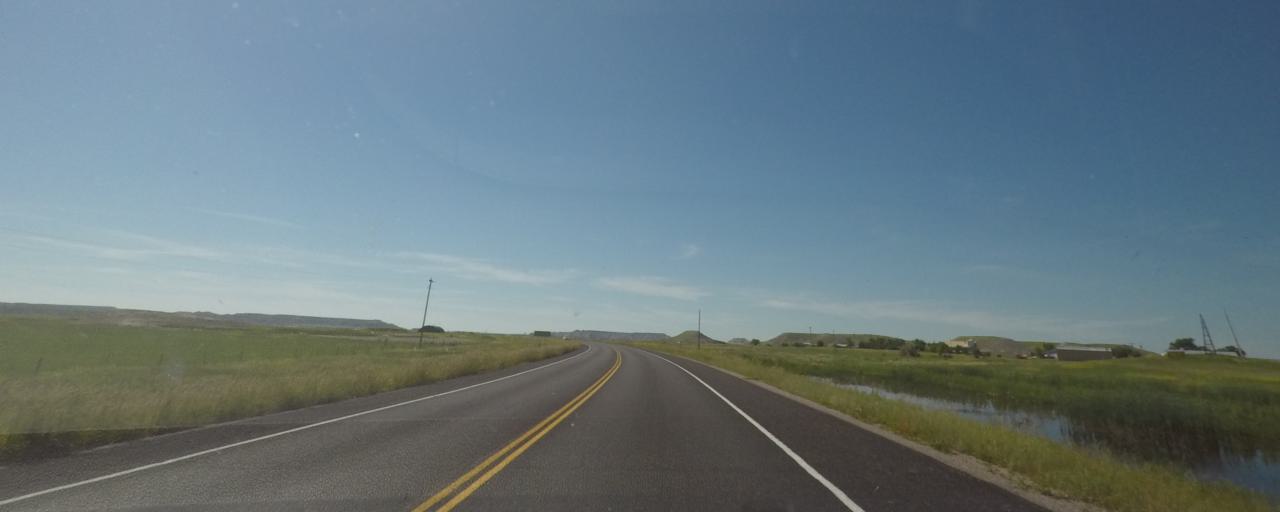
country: US
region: South Dakota
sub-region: Shannon County
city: Porcupine
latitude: 43.7834
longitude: -102.5539
